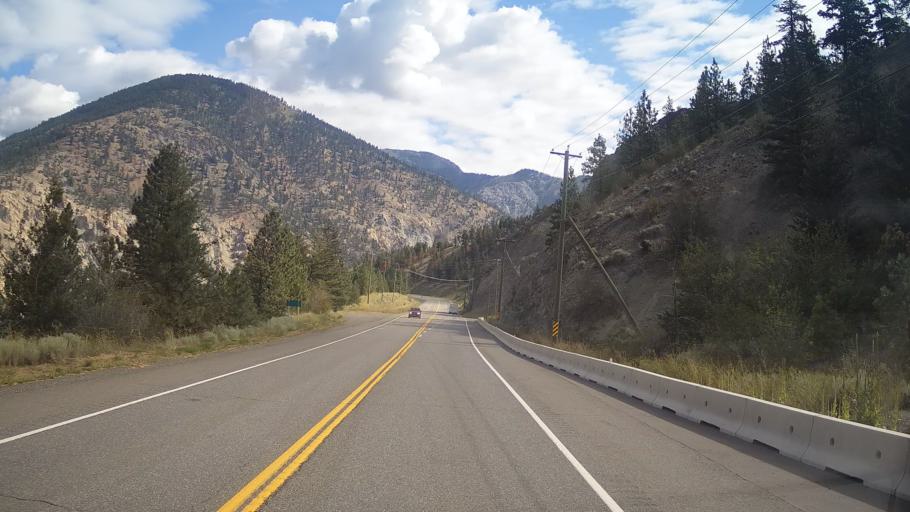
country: CA
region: British Columbia
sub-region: Thompson-Nicola Regional District
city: Ashcroft
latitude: 50.2522
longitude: -121.5485
